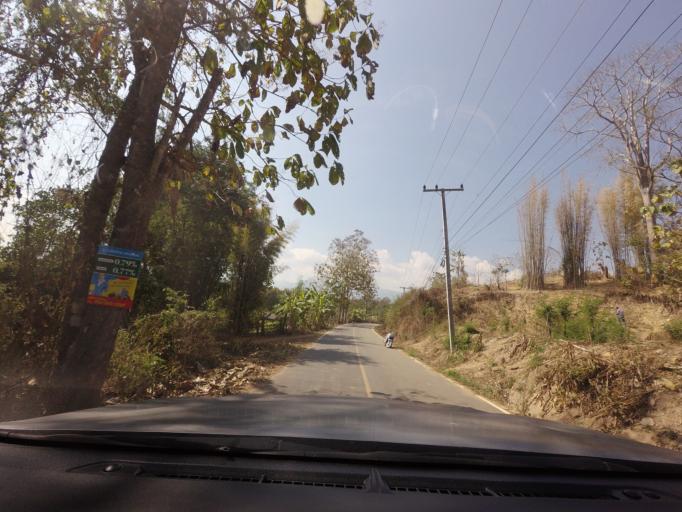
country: TH
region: Mae Hong Son
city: Wiang Nuea
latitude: 19.4026
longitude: 98.4463
